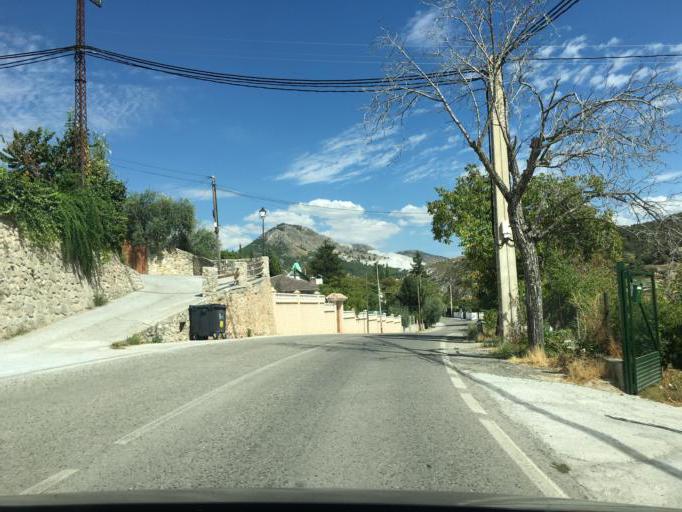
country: ES
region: Andalusia
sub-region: Provincia de Granada
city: Huetor Santillan
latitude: 37.2239
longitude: -3.5109
